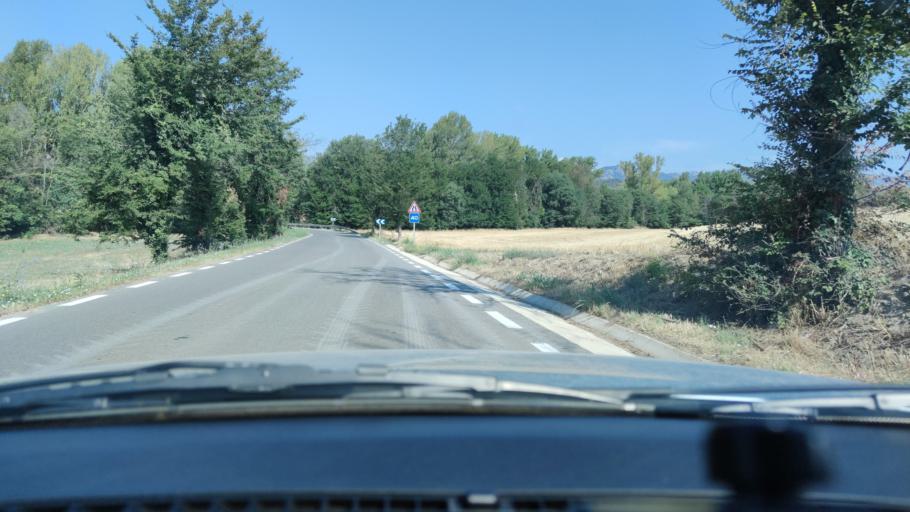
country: ES
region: Catalonia
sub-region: Provincia de Lleida
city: Tremp
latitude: 42.2118
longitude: 0.9409
